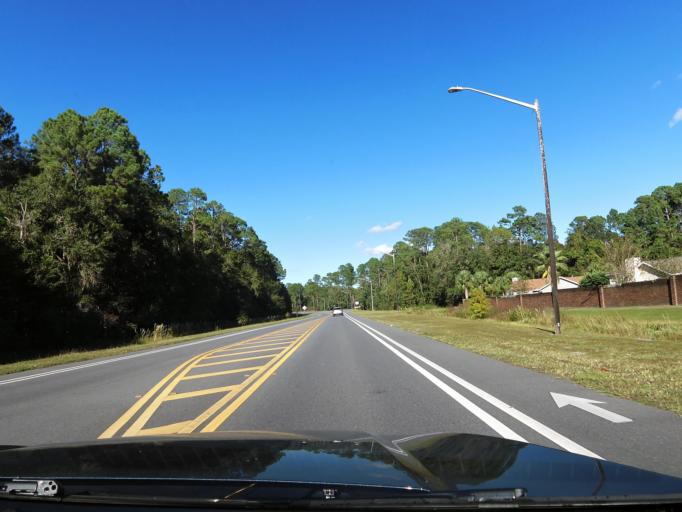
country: US
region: Florida
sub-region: Alachua County
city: Alachua
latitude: 29.7127
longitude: -82.3872
